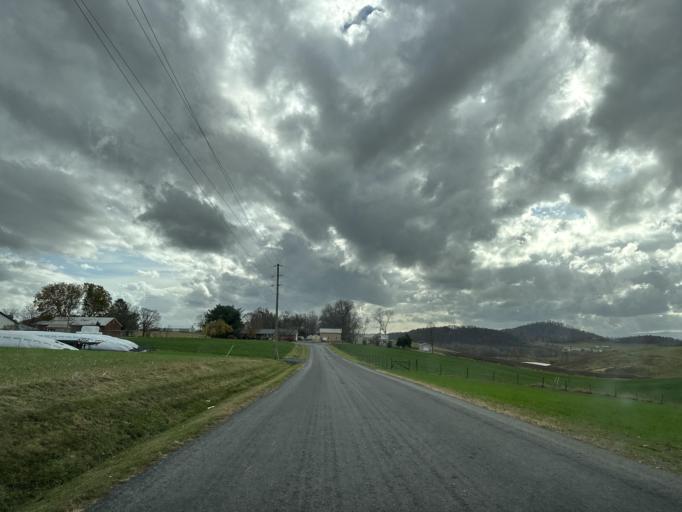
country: US
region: Virginia
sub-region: Rockingham County
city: Dayton
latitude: 38.4158
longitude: -78.9672
